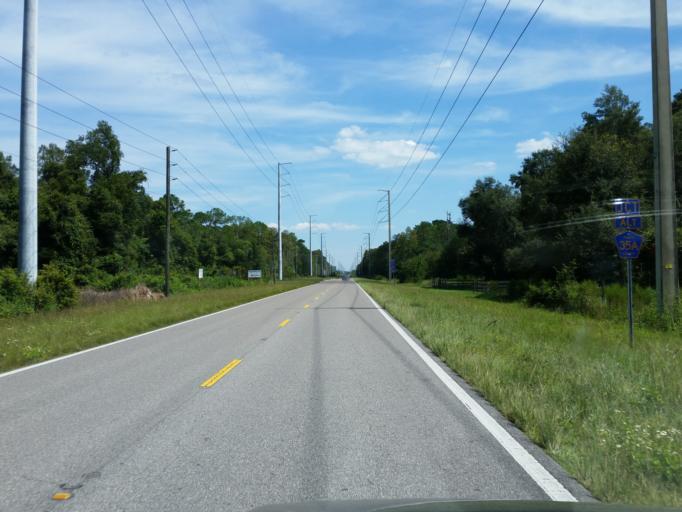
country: US
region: Florida
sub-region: Pasco County
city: Zephyrhills North
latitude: 28.2592
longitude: -82.1149
